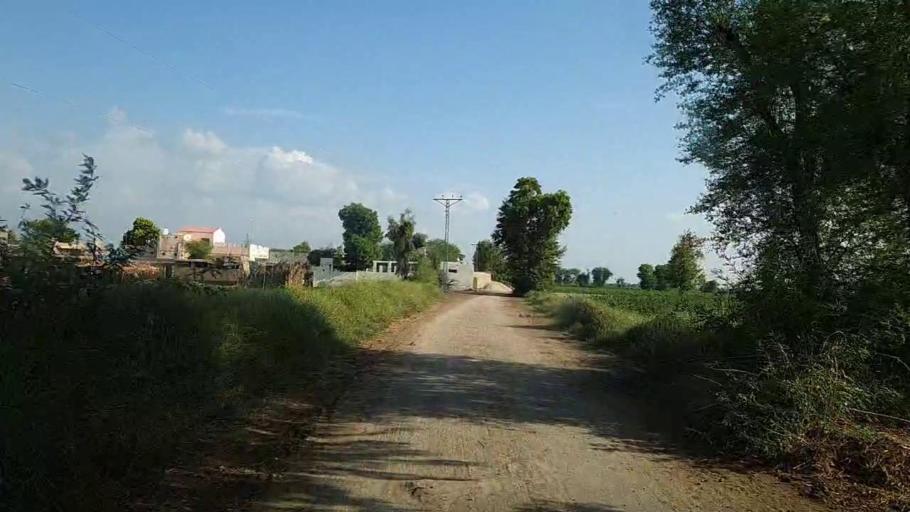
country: PK
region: Sindh
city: Hingorja
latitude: 27.0927
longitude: 68.3648
